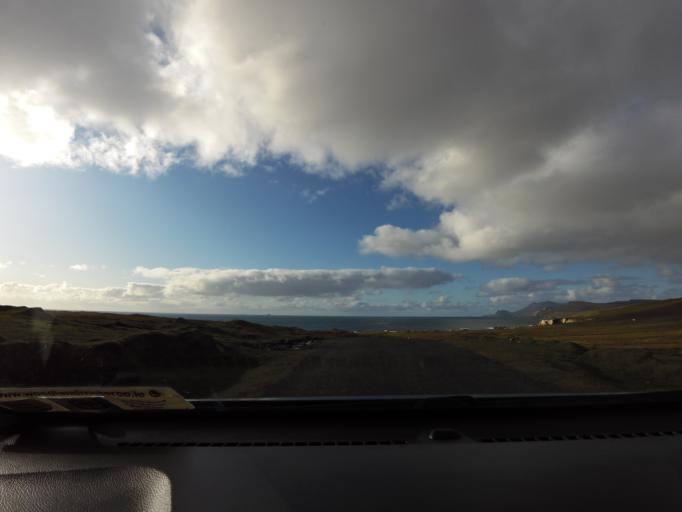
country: IE
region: Connaught
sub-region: Maigh Eo
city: Belmullet
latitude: 53.8883
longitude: -9.9833
